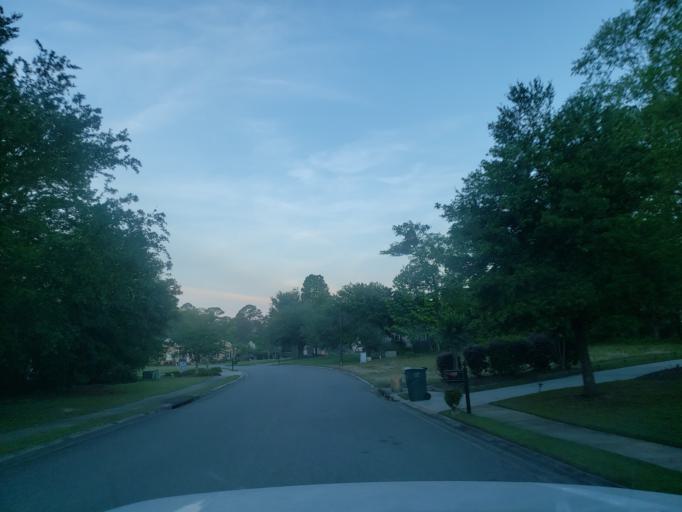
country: US
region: Georgia
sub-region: Chatham County
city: Pooler
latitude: 32.0704
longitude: -81.2432
